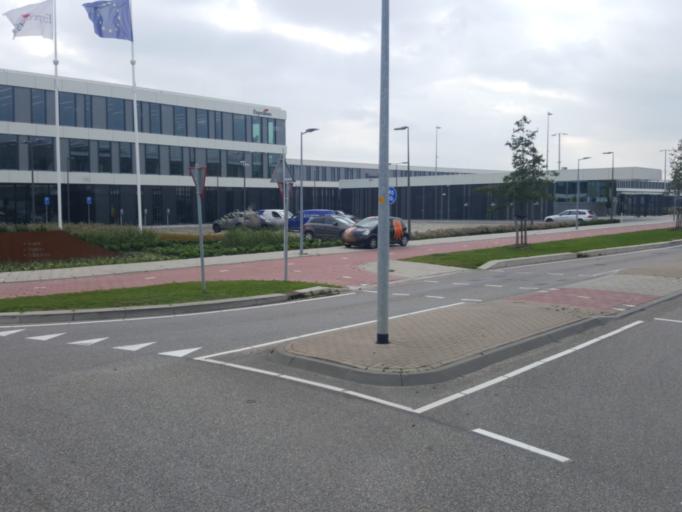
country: NL
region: North Holland
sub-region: Gemeente Aalsmeer
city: Aalsmeer
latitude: 52.2744
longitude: 4.7414
